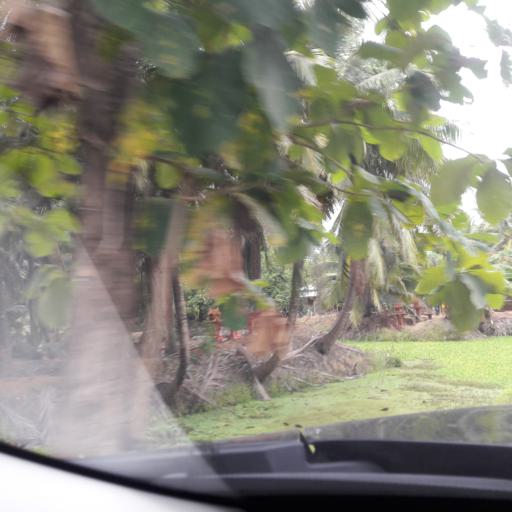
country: TH
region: Ratchaburi
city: Damnoen Saduak
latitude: 13.5730
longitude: 99.9523
